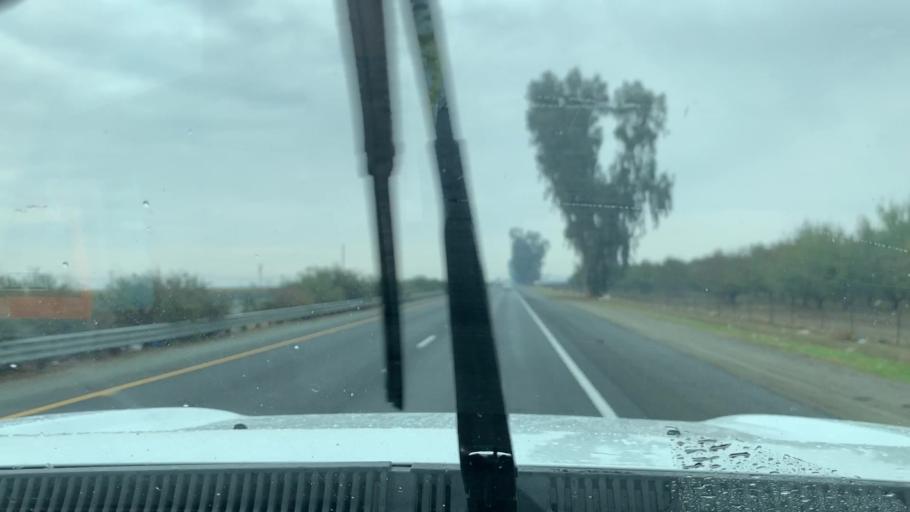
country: US
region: California
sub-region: Kern County
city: Delano
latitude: 35.8023
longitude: -119.2551
